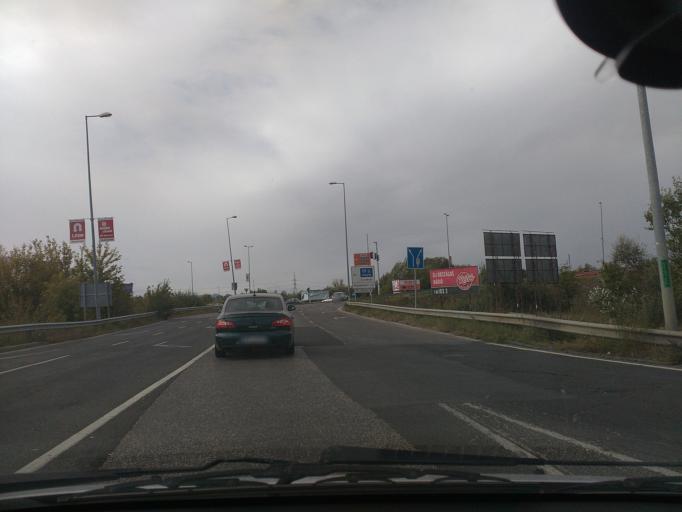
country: HU
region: Budapest
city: Budapest XVIII. keruelet
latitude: 47.4244
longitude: 19.1564
